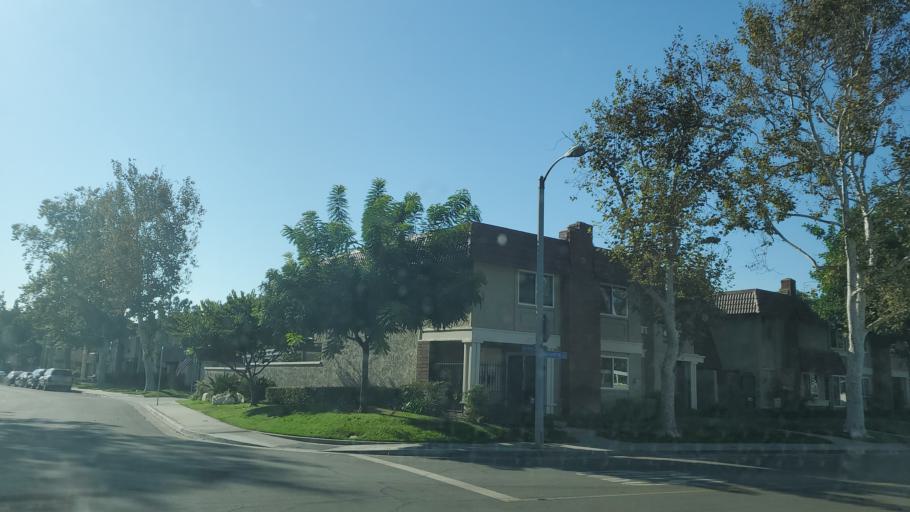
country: US
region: California
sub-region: Orange County
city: Stanton
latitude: 33.7979
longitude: -118.0131
